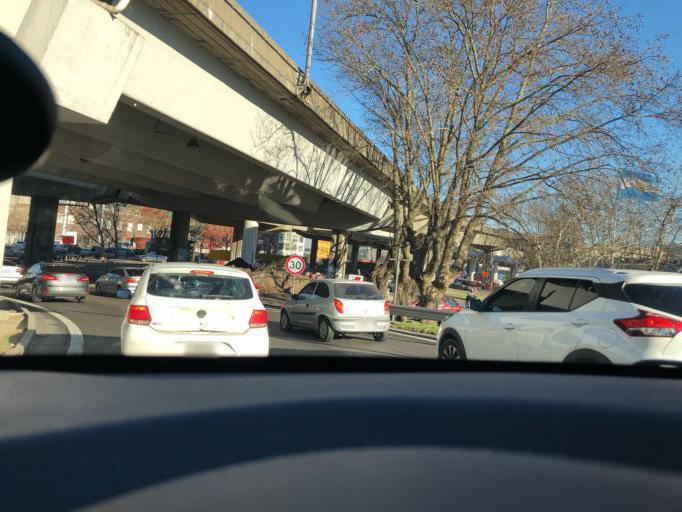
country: AR
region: Buenos Aires F.D.
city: Buenos Aires
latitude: -34.6248
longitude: -58.3624
